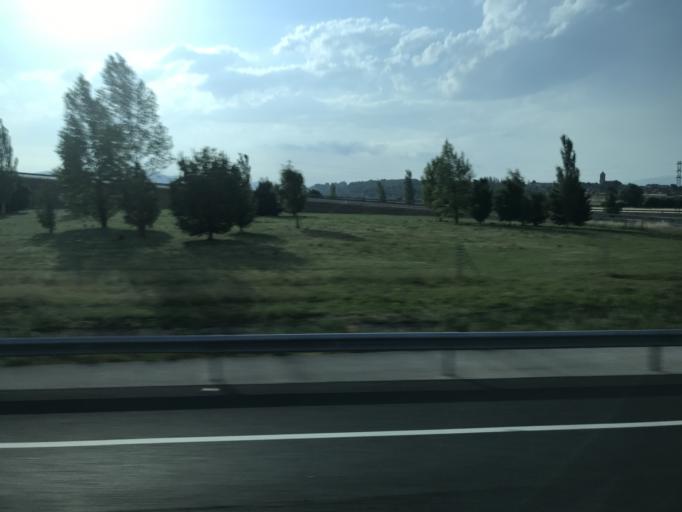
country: ES
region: Basque Country
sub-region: Provincia de Alava
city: Gasteiz / Vitoria
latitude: 42.9085
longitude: -2.7047
